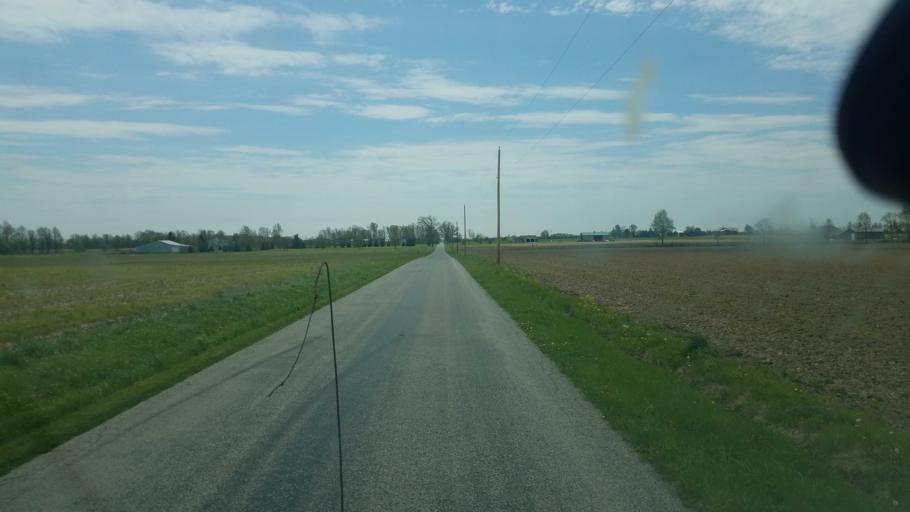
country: US
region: Ohio
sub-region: Allen County
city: Bluffton
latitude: 40.8074
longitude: -83.9087
